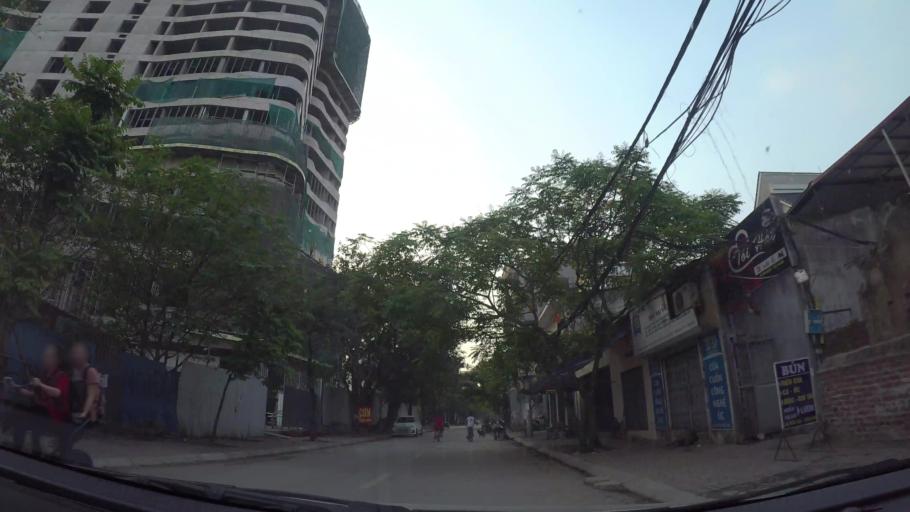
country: VN
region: Ha Noi
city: Tay Ho
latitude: 21.0670
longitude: 105.7893
